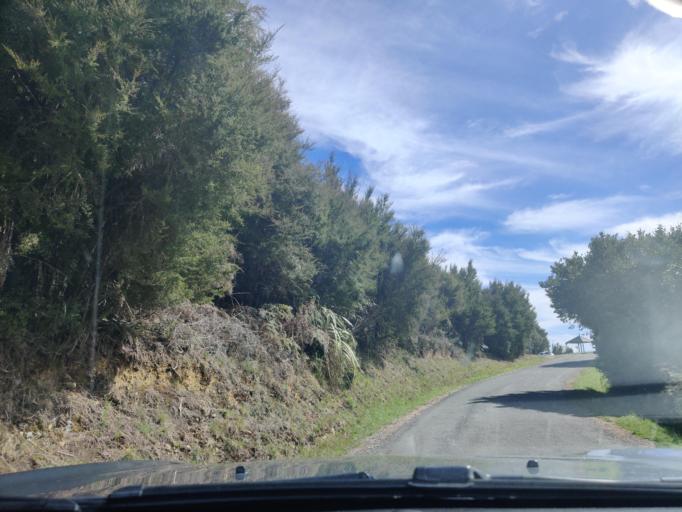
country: NZ
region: Tasman
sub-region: Tasman District
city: Wakefield
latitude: -41.6284
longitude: 172.7197
